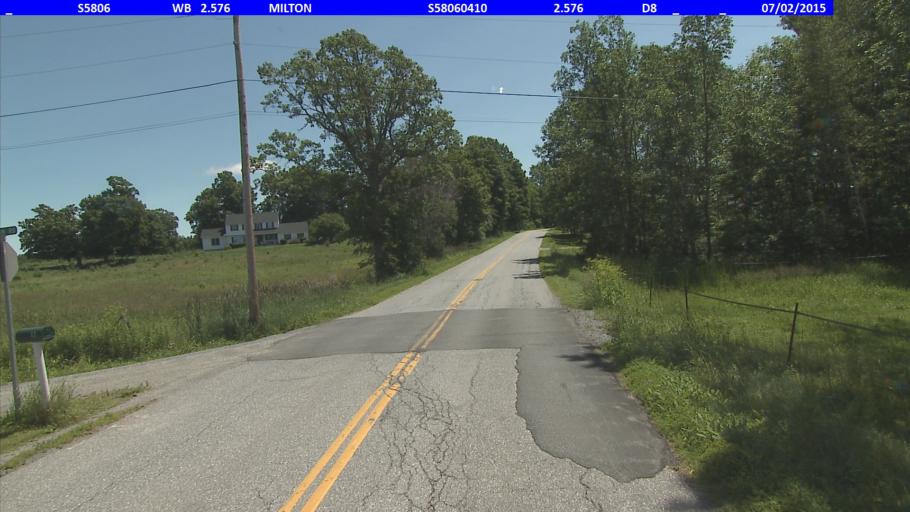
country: US
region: Vermont
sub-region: Chittenden County
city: Milton
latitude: 44.6665
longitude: -73.1592
